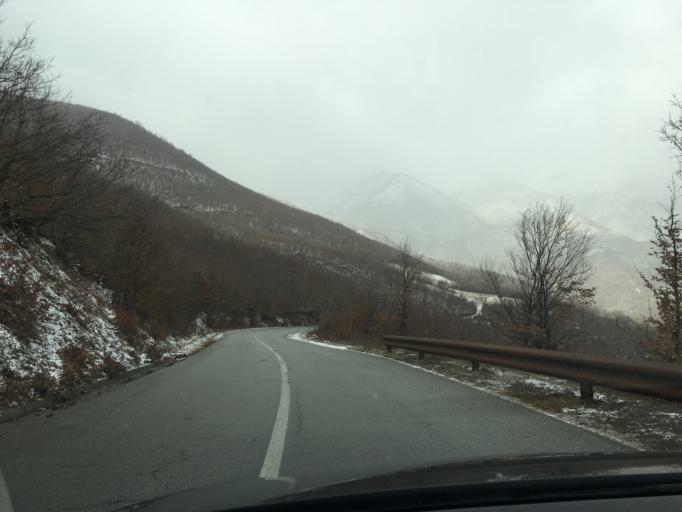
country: XK
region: Pec
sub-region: Komuna e Pejes
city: Dubova (Driloni)
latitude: 42.7504
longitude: 20.3039
